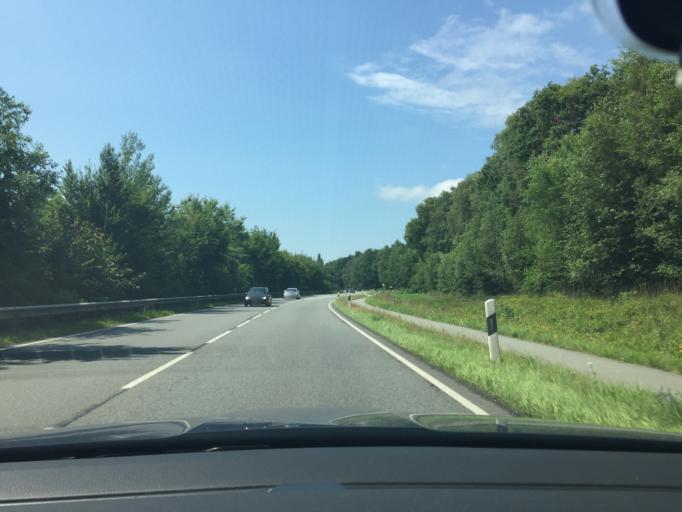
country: DE
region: Lower Saxony
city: Wardenburg
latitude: 53.1061
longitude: 8.1179
